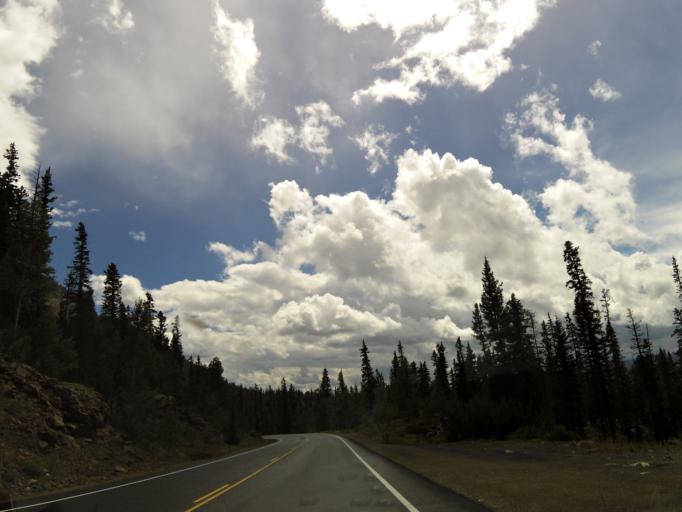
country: US
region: Colorado
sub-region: San Juan County
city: Silverton
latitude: 37.6844
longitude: -107.7794
